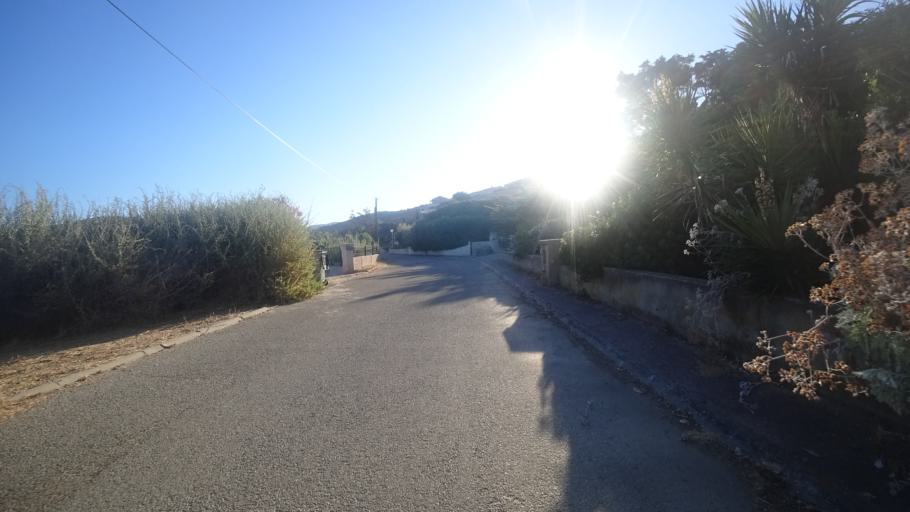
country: FR
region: Corsica
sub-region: Departement de la Corse-du-Sud
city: Alata
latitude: 41.9801
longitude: 8.6671
